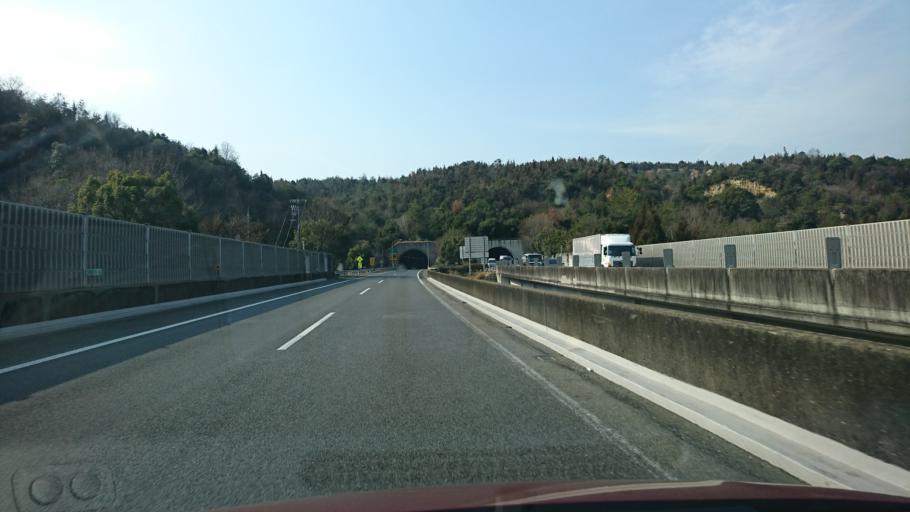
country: JP
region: Hiroshima
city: Fukuyama
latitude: 34.4817
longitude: 133.3087
